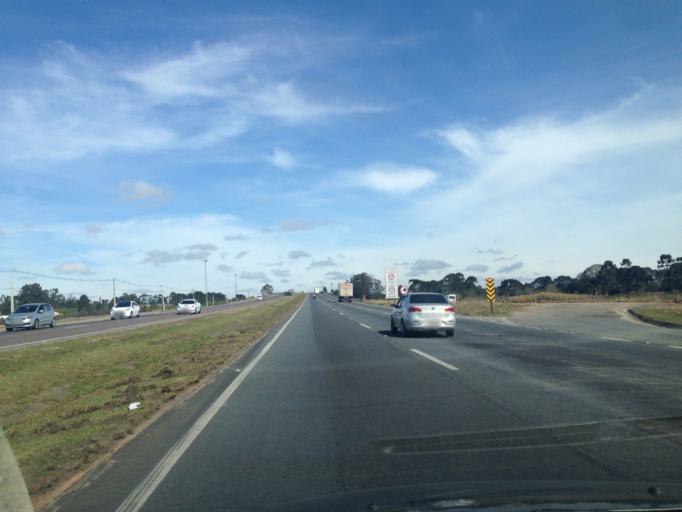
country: BR
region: Parana
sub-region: Sao Jose Dos Pinhais
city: Sao Jose dos Pinhais
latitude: -25.5288
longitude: -49.1421
